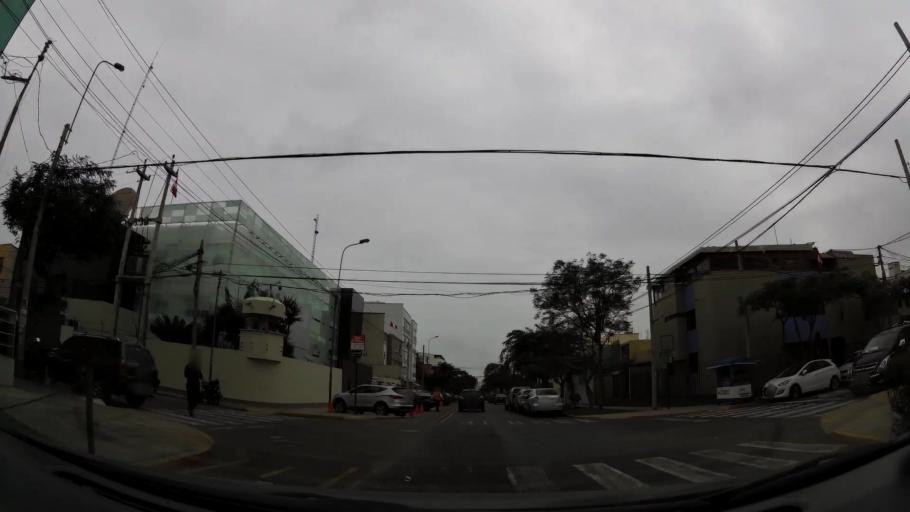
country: PE
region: Lima
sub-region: Lima
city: San Isidro
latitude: -12.0900
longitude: -77.0399
